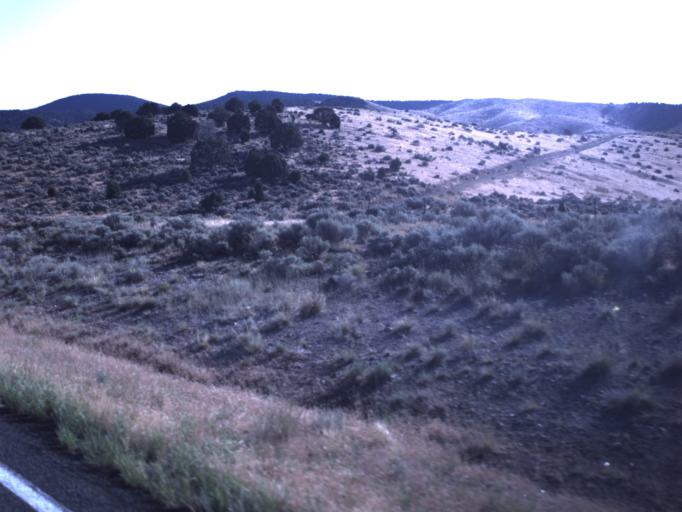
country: US
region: Utah
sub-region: Iron County
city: Parowan
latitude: 38.0992
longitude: -112.9494
